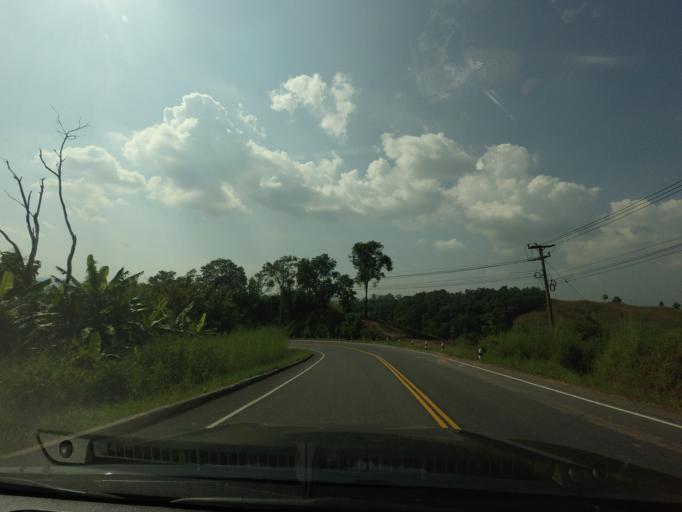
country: TH
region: Nan
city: Santi Suk
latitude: 18.9828
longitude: 100.9502
